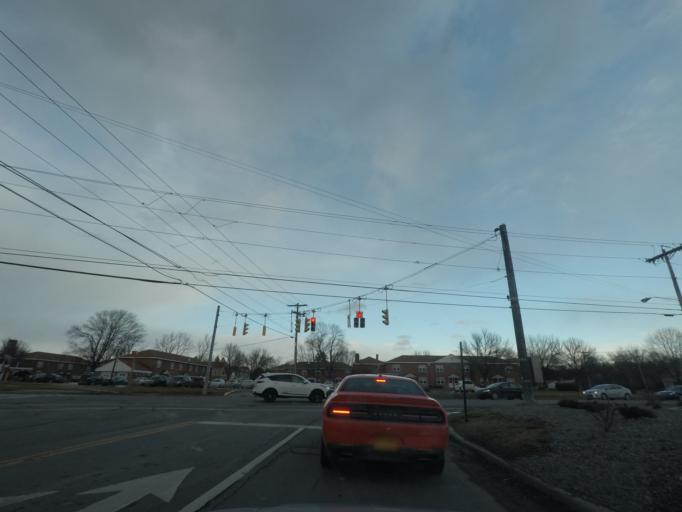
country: US
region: New York
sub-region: Oneida County
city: Utica
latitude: 43.1145
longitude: -75.2057
